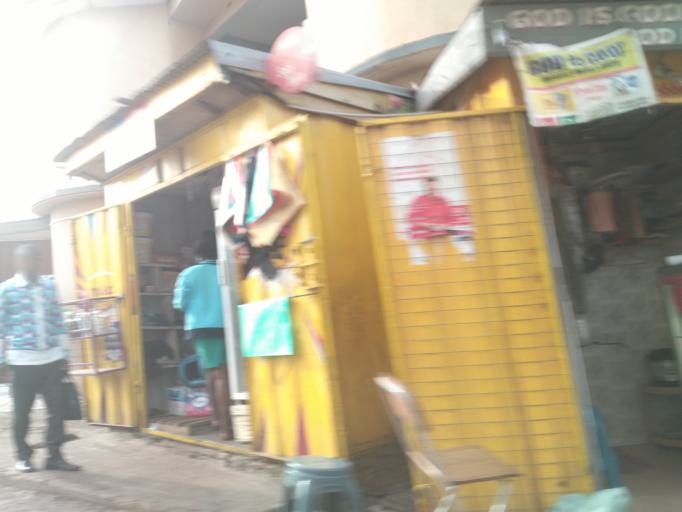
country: GH
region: Ashanti
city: Kumasi
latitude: 6.6905
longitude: -1.6109
